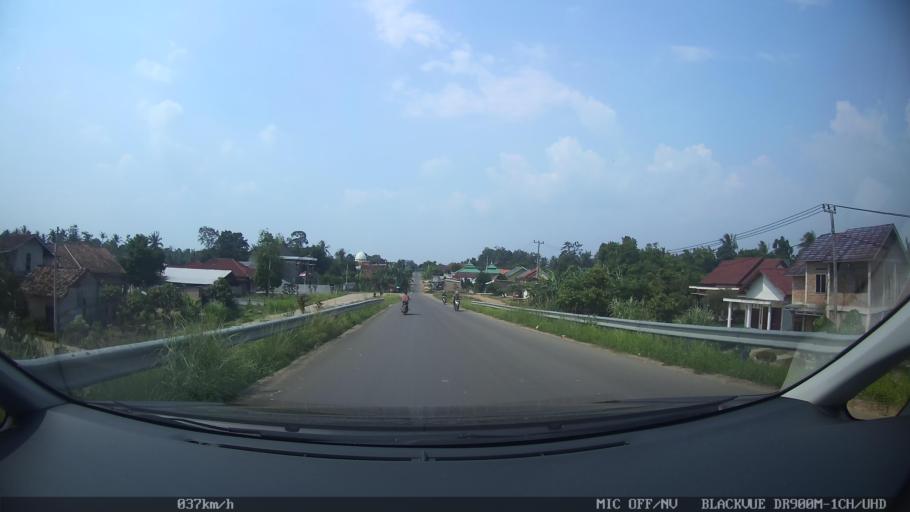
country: ID
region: Lampung
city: Natar
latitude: -5.3003
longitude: 105.2427
